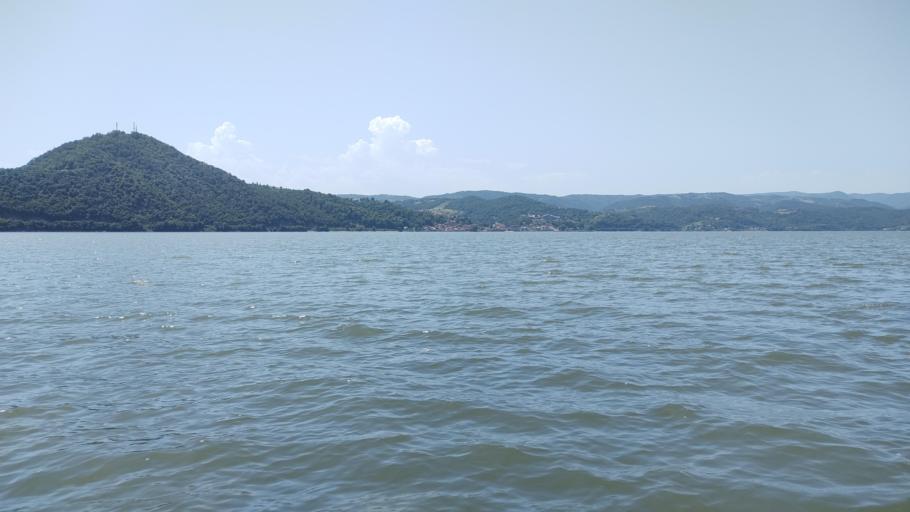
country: RO
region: Mehedinti
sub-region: Comuna Svinita
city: Svinita
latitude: 44.4805
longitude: 22.1711
